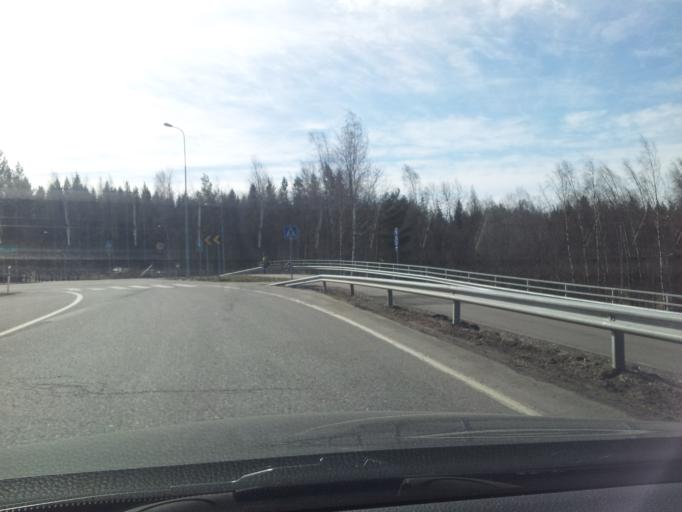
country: FI
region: Uusimaa
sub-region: Helsinki
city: Kirkkonummi
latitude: 60.1369
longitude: 24.5347
